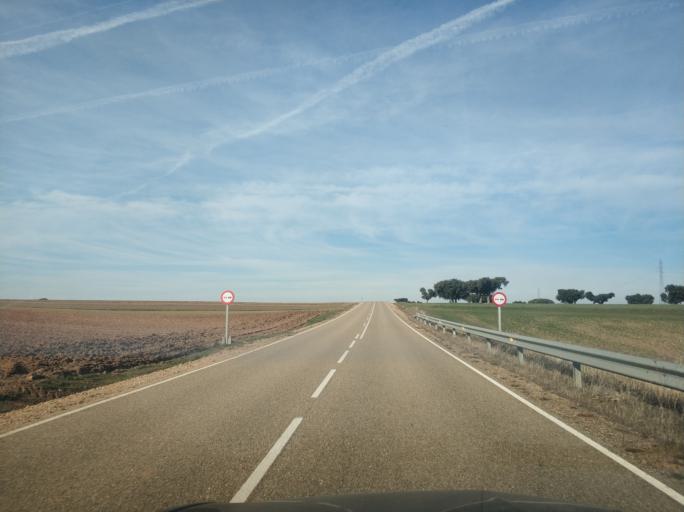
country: ES
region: Castille and Leon
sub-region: Provincia de Salamanca
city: Parada de Arriba
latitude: 40.9953
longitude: -5.8136
